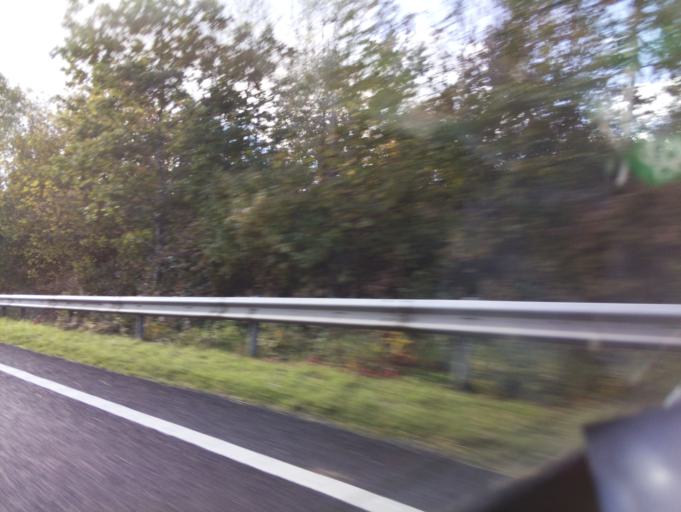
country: GB
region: Wales
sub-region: Sir Powys
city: Brecon
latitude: 51.9885
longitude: -3.3256
